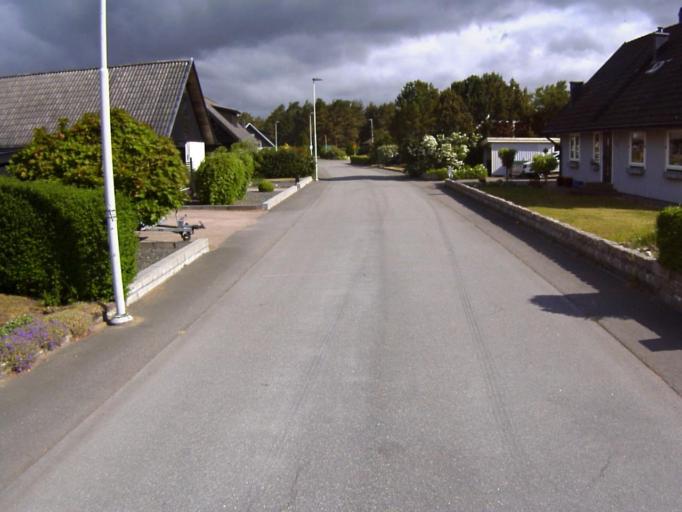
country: SE
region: Skane
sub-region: Kristianstads Kommun
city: Ahus
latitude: 55.9357
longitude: 14.2810
